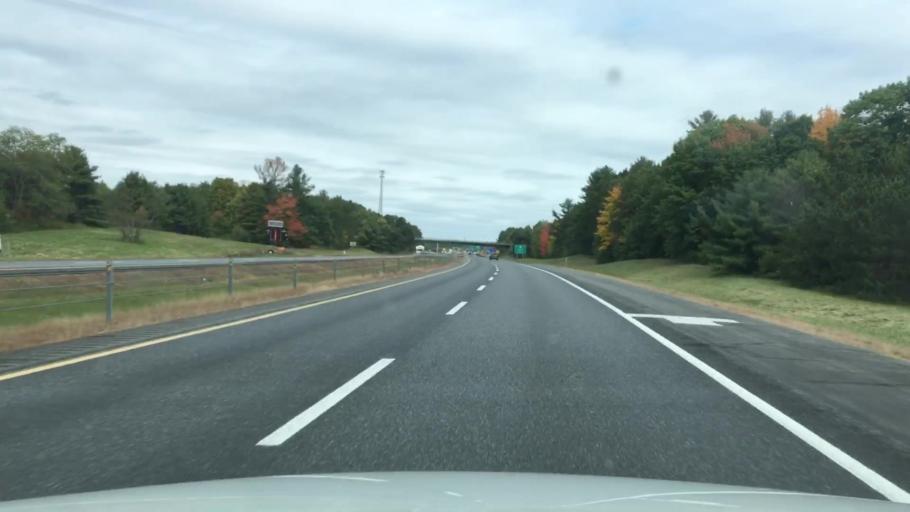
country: US
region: Maine
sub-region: Kennebec County
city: Gardiner
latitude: 44.1975
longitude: -69.8257
